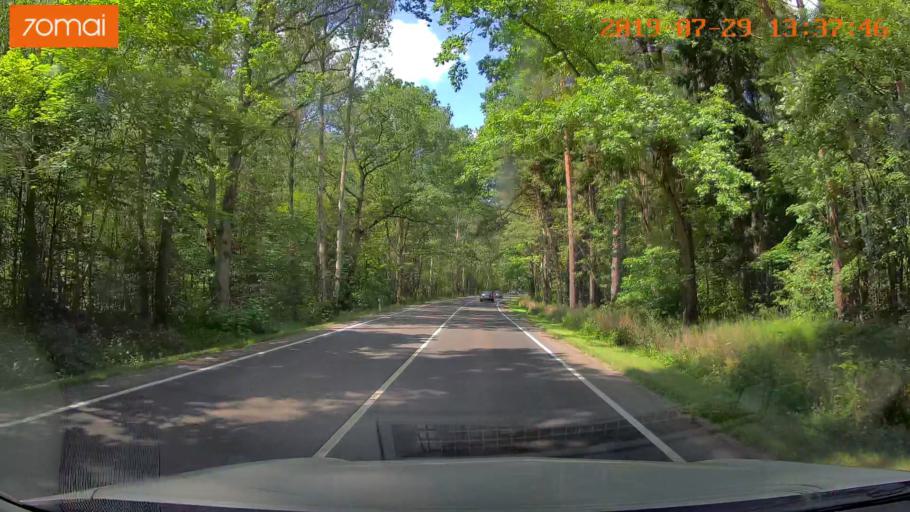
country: RU
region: Kaliningrad
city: Volochayevskoye
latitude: 54.7163
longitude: 20.1795
